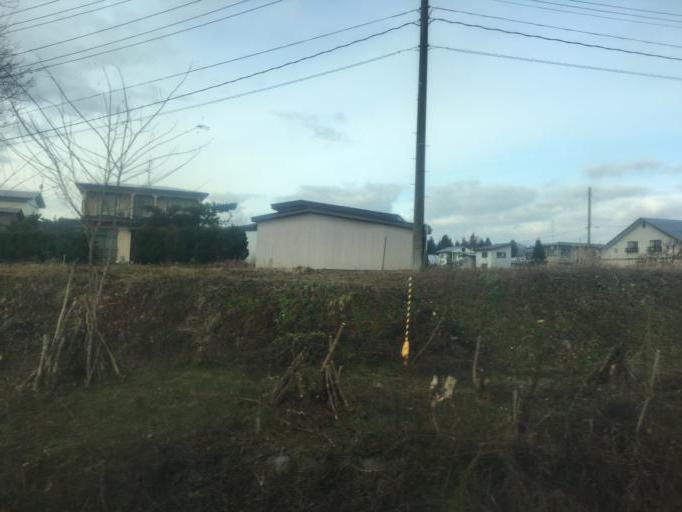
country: JP
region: Akita
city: Odate
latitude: 40.3000
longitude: 140.5673
